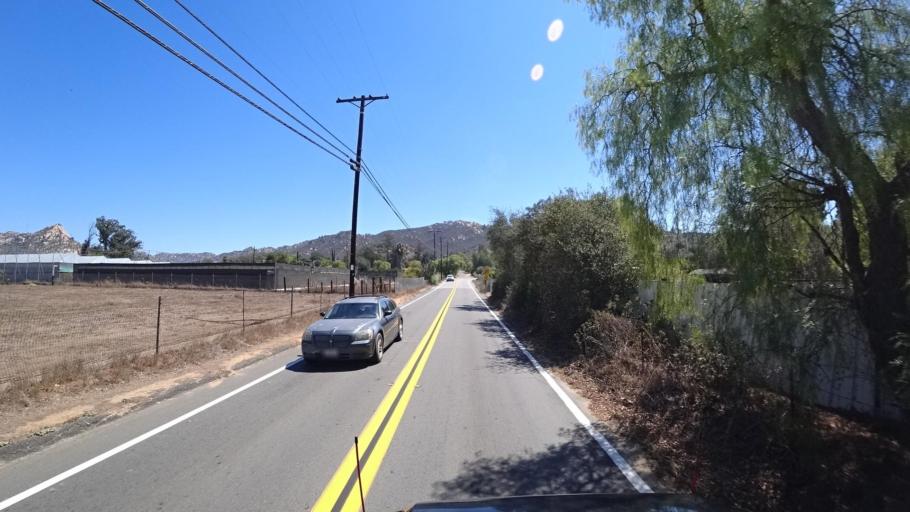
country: US
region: California
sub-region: San Diego County
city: Rainbow
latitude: 33.4104
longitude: -117.1469
